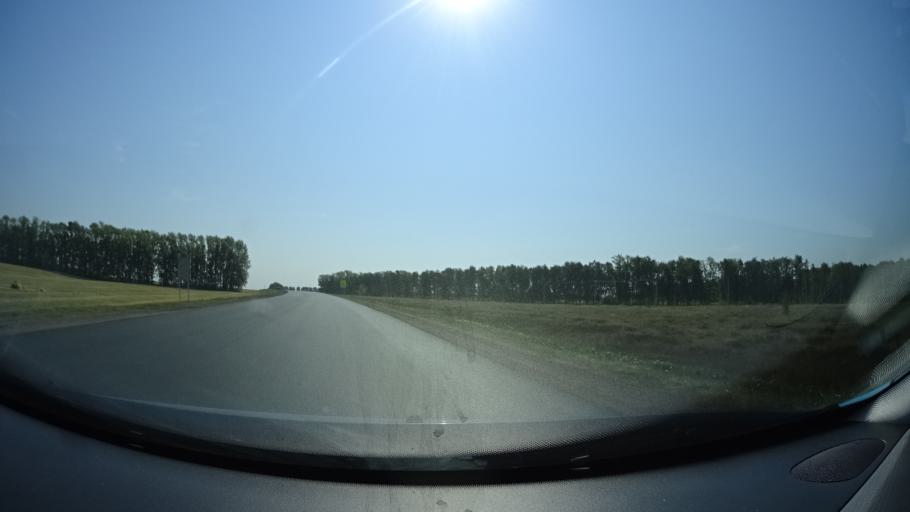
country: RU
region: Bashkortostan
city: Kabakovo
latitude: 54.4812
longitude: 55.9246
